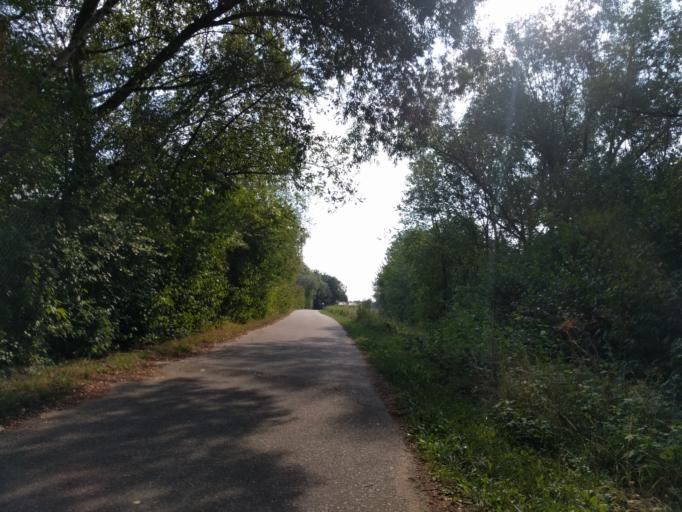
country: DE
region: Bavaria
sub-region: Upper Palatinate
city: Tegernheim
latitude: 49.0190
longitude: 12.1632
